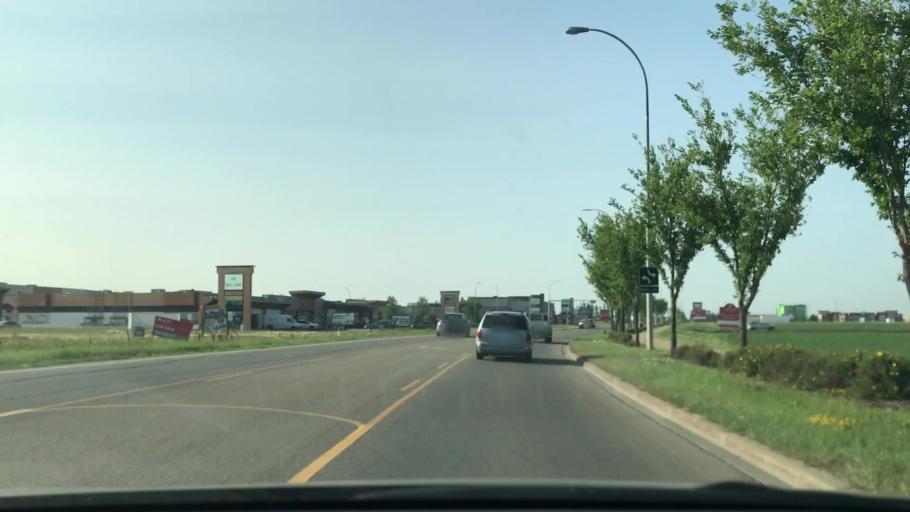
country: CA
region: Alberta
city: Beaumont
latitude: 53.4313
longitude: -113.4801
